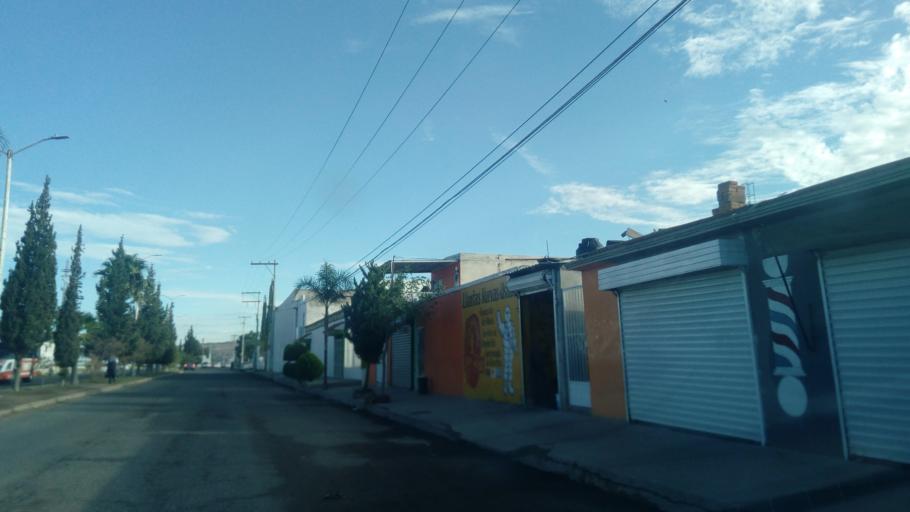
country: MX
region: Durango
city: Victoria de Durango
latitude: 24.0557
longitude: -104.6100
